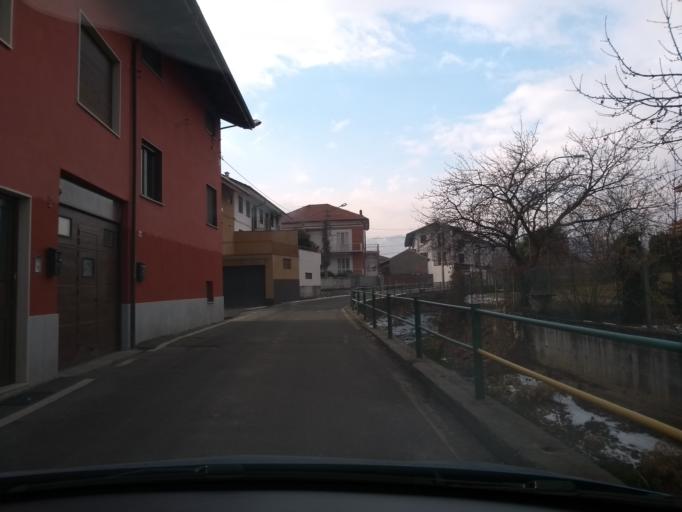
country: IT
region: Piedmont
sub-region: Provincia di Torino
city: Balangero
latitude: 45.2721
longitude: 7.5195
